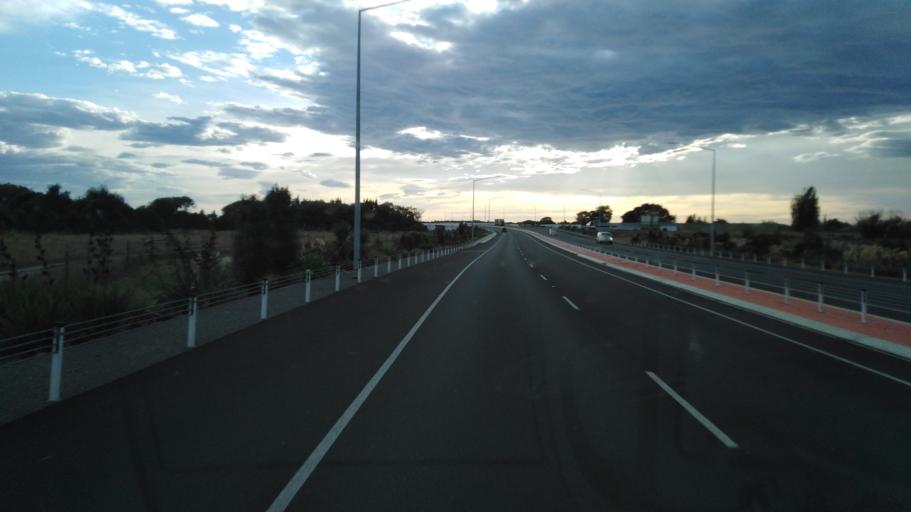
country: NZ
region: Canterbury
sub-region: Waimakariri District
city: Kaiapoi
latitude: -43.4377
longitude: 172.6281
